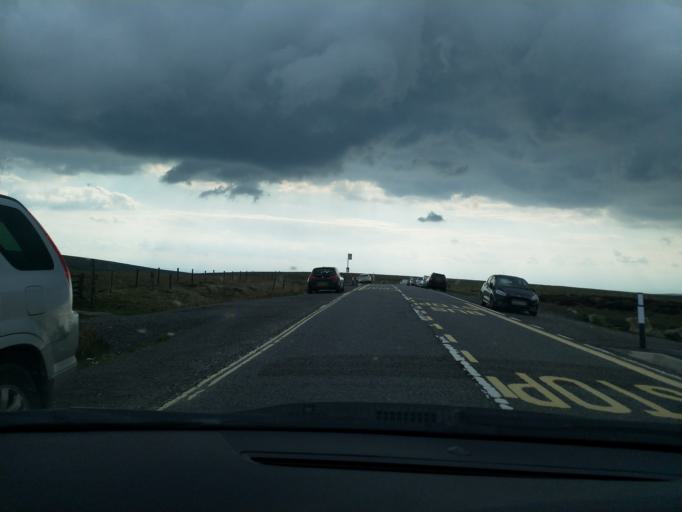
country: GB
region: England
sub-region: Derbyshire
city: High Peak
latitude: 53.4329
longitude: -1.8685
